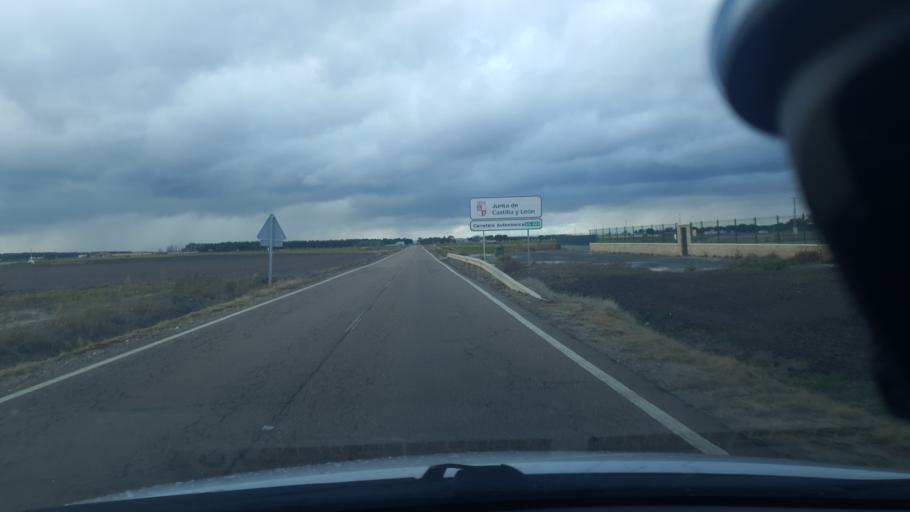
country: ES
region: Castille and Leon
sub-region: Provincia de Segovia
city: Sanchonuno
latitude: 41.2941
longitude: -4.3321
